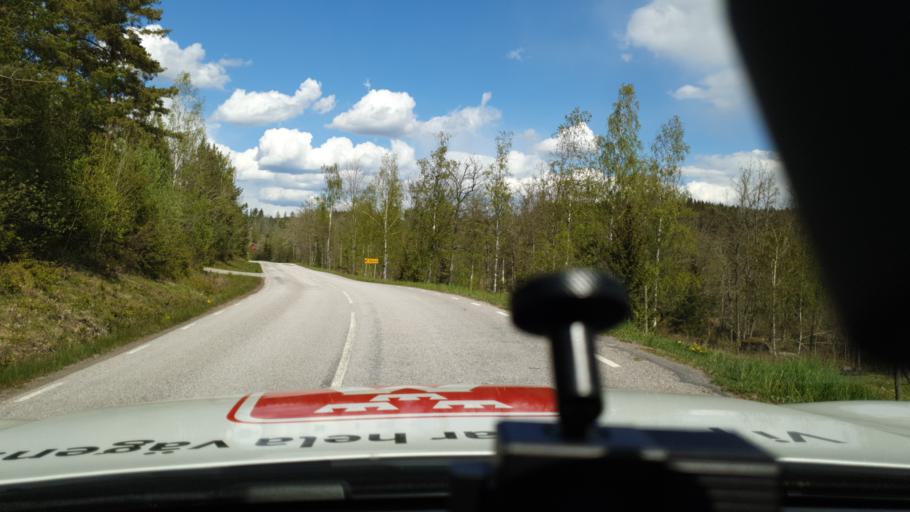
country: SE
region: Kalmar
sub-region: Vasterviks Kommun
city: Ankarsrum
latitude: 57.8186
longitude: 16.2379
